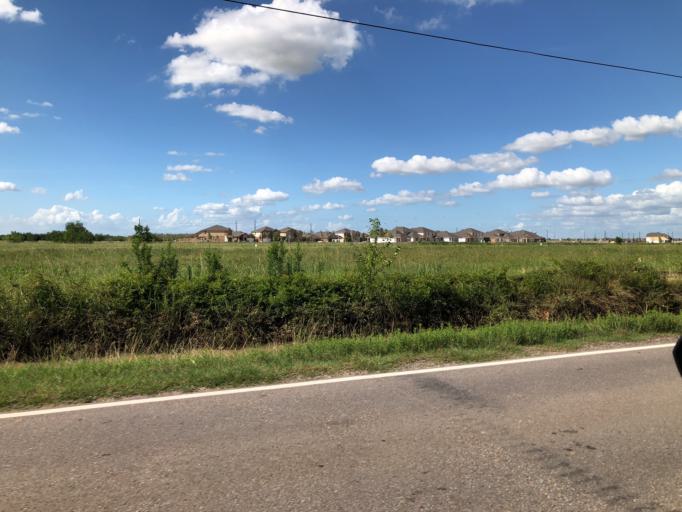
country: US
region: Texas
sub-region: Harris County
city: Katy
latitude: 29.8314
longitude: -95.7969
